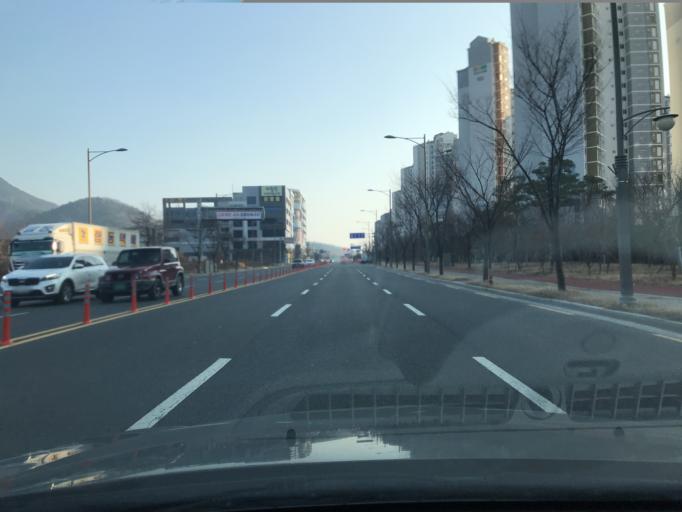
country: KR
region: Daegu
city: Hwawon
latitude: 35.6963
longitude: 128.4698
